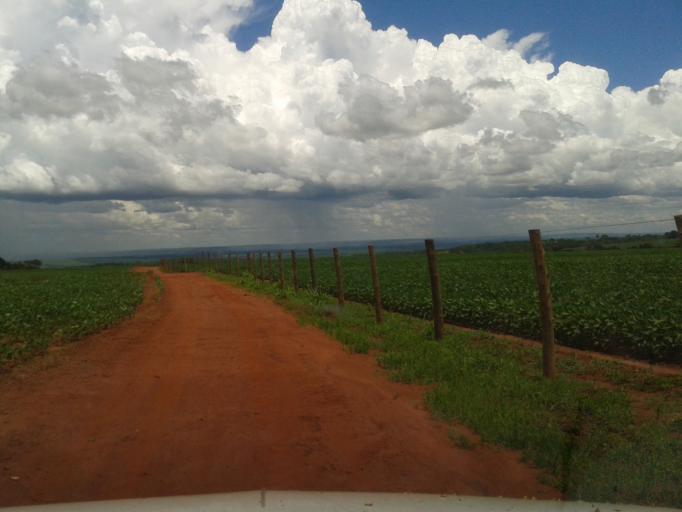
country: BR
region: Minas Gerais
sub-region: Centralina
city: Centralina
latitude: -18.6674
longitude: -49.1749
